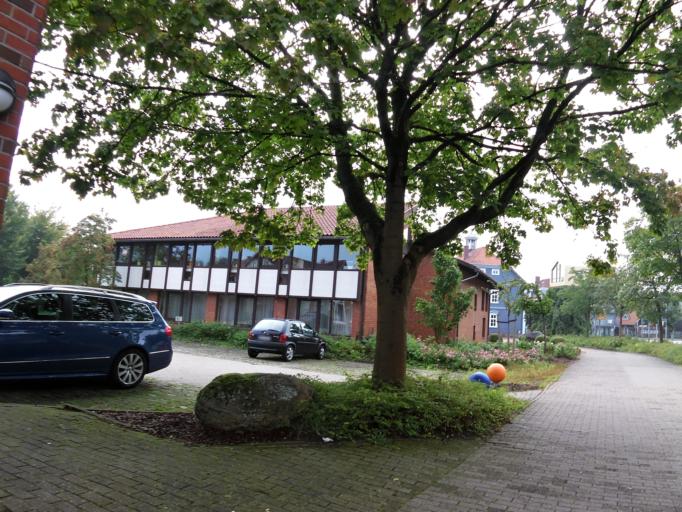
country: DE
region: Lower Saxony
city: Soltau
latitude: 52.9878
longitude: 9.8372
